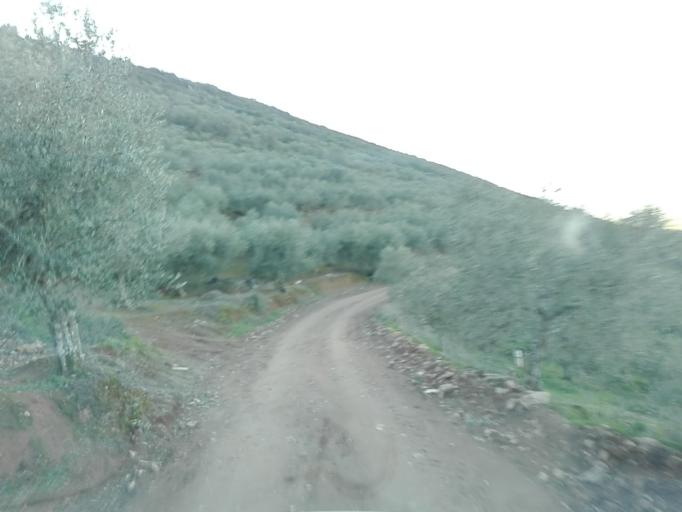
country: ES
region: Extremadura
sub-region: Provincia de Badajoz
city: Llerena
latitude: 38.2147
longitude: -5.9988
